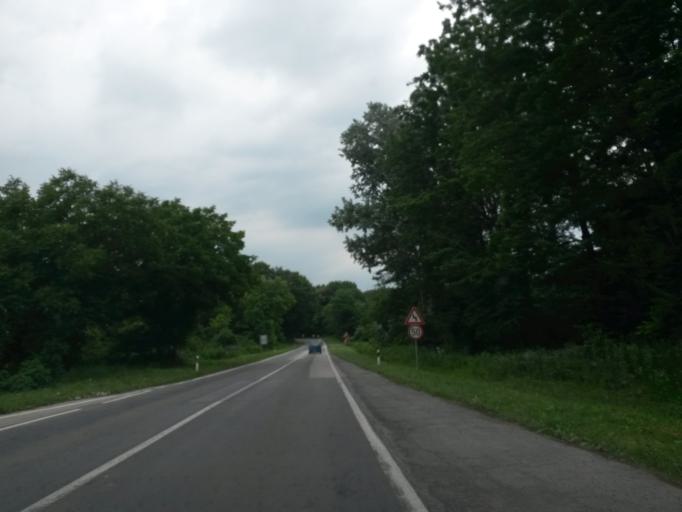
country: HR
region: Vukovarsko-Srijemska
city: Vukovar
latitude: 45.3296
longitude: 19.0436
